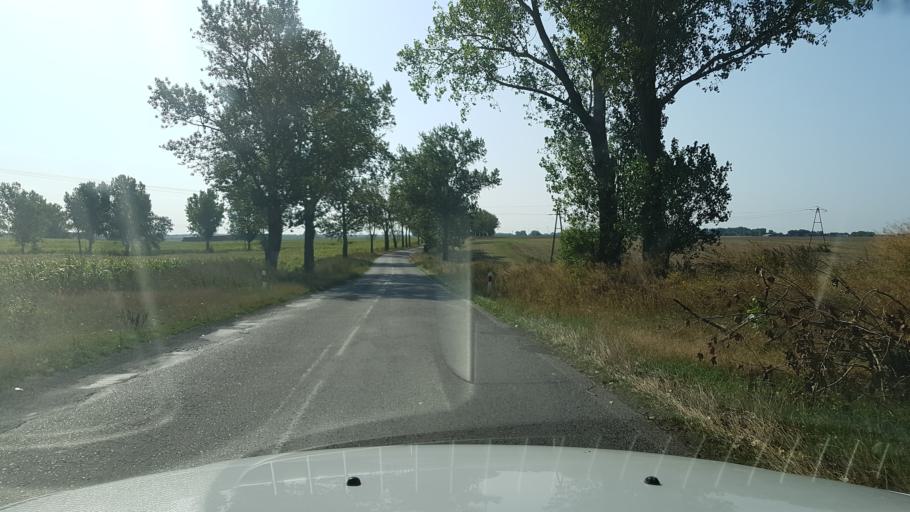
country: PL
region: West Pomeranian Voivodeship
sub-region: Powiat stargardzki
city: Stargard Szczecinski
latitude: 53.2724
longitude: 15.0858
